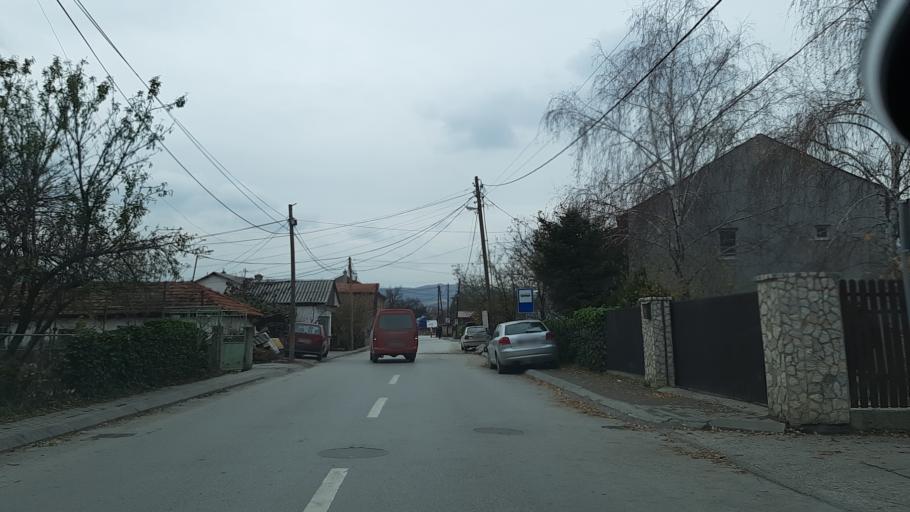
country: MK
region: Kisela Voda
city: Usje
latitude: 41.9751
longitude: 21.4803
